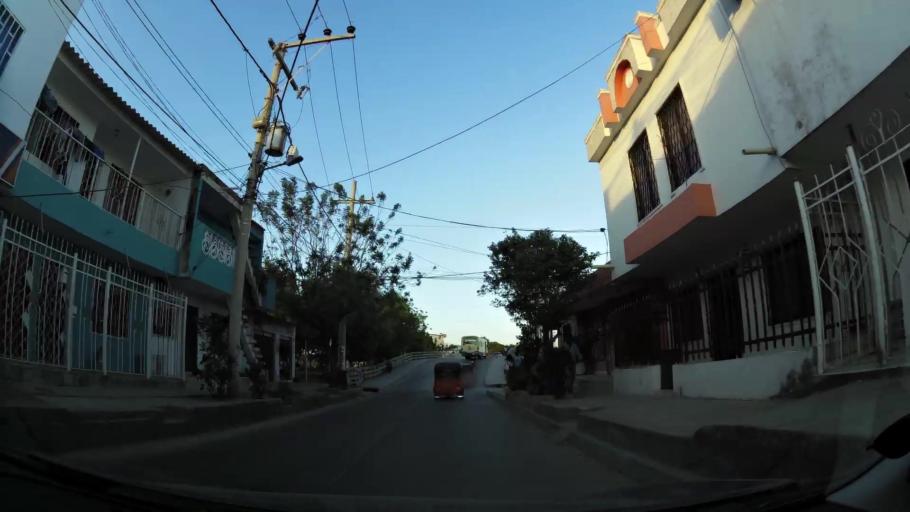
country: CO
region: Atlantico
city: Soledad
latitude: 10.9241
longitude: -74.7860
